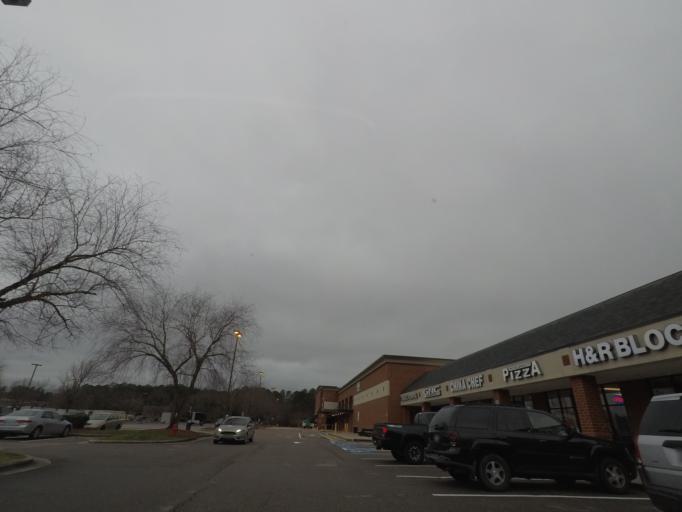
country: US
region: North Carolina
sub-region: Wake County
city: Apex
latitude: 35.7455
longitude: -78.8211
